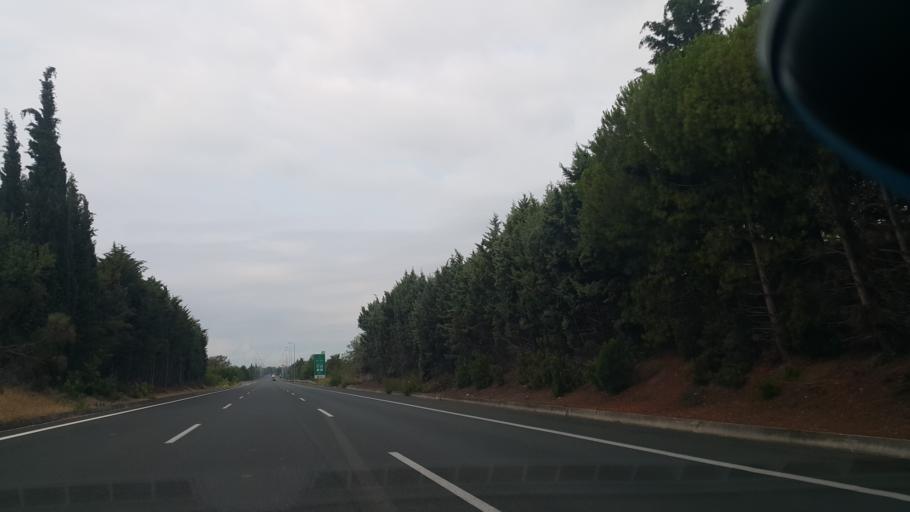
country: GR
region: Central Macedonia
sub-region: Nomos Pierias
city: Korinos
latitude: 40.3388
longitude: 22.5873
